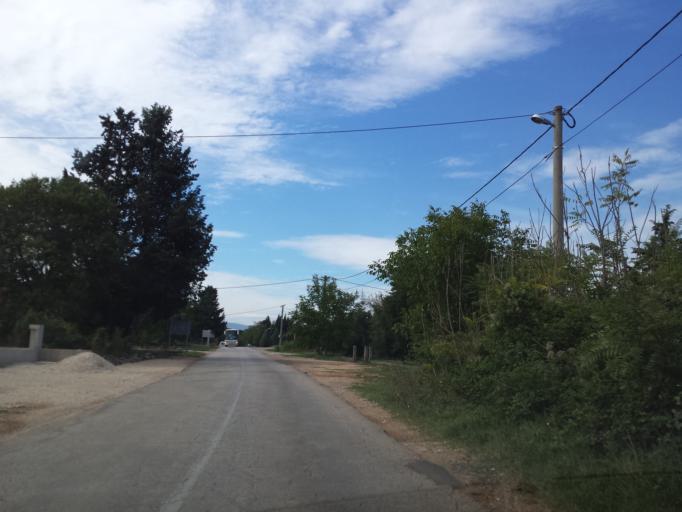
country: BA
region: Federation of Bosnia and Herzegovina
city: Citluk
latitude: 43.1935
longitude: 17.6546
